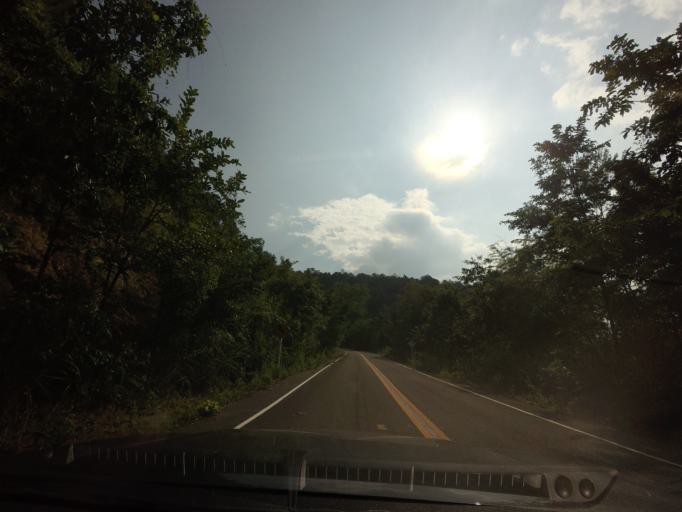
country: TH
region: Nan
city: Na Noi
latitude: 18.2804
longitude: 100.9531
